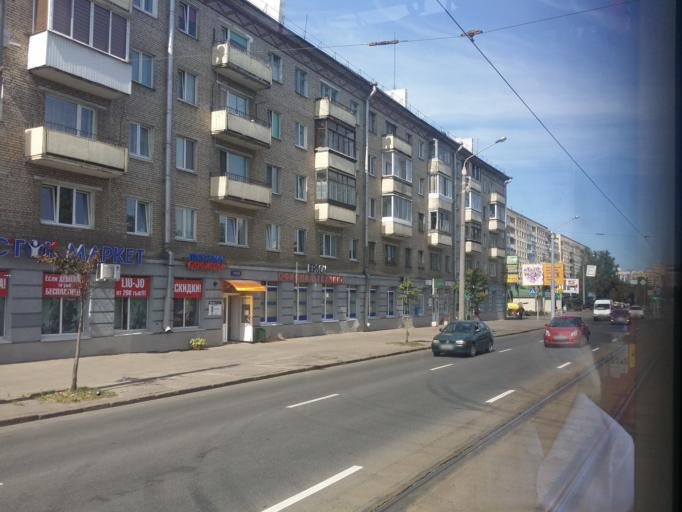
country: BY
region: Minsk
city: Minsk
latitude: 53.9347
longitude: 27.6024
